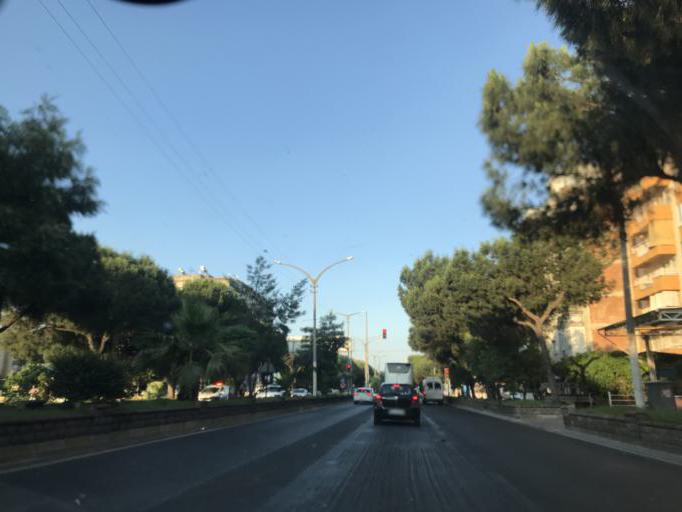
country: TR
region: Aydin
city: Nazilli
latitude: 37.9098
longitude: 28.3262
